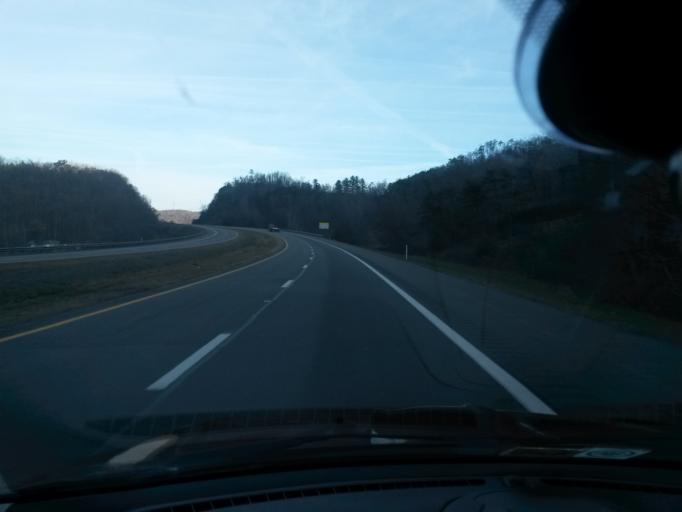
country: US
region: West Virginia
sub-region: Greenbrier County
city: Lewisburg
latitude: 37.7805
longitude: -80.3815
